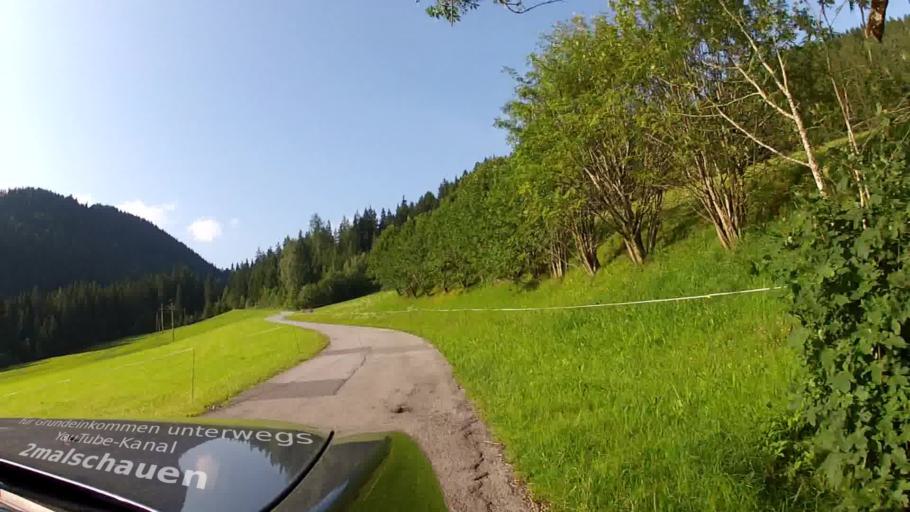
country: AT
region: Salzburg
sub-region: Politischer Bezirk Sankt Johann im Pongau
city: Eben im Pongau
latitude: 47.4295
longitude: 13.3811
